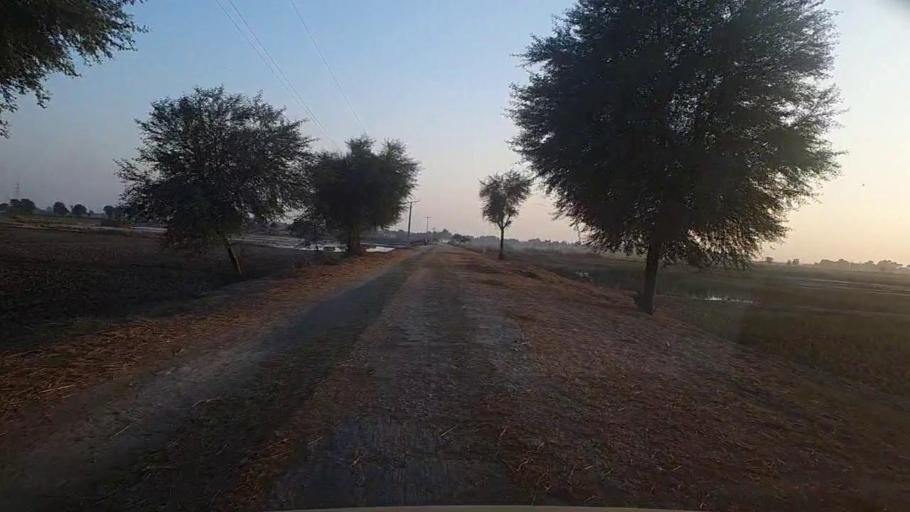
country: PK
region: Sindh
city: Khairpur Nathan Shah
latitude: 27.1664
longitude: 67.7324
